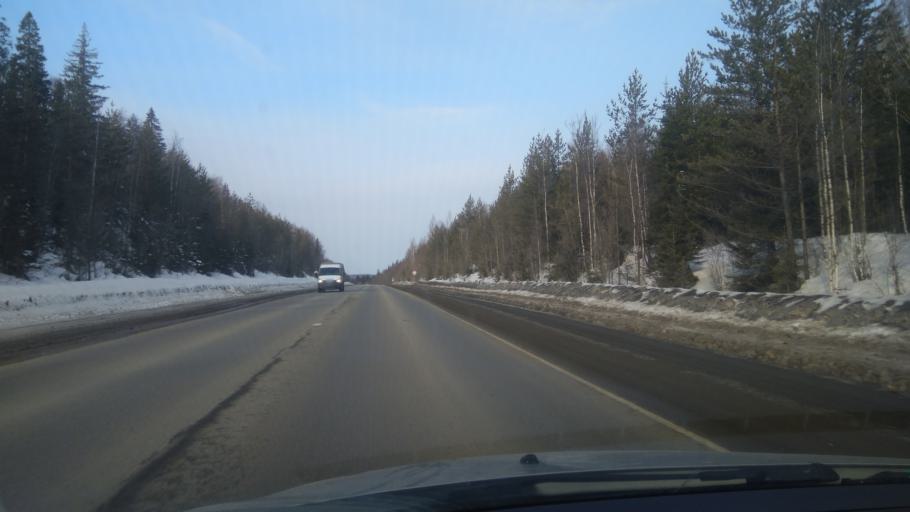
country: RU
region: Sverdlovsk
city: Bisert'
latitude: 56.8269
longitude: 59.2145
